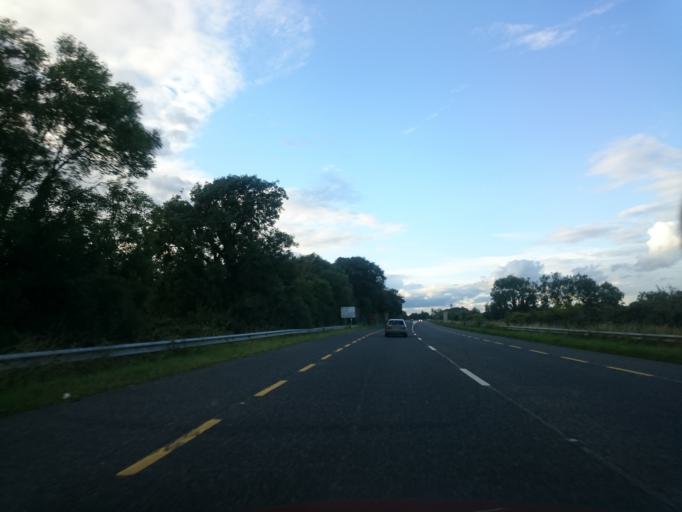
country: IE
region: Leinster
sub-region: Loch Garman
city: Castlebridge
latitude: 52.3796
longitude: -6.5198
